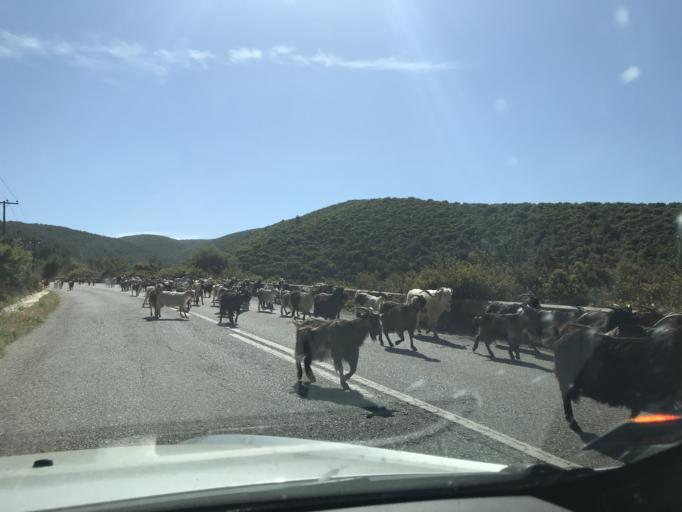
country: GR
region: Central Macedonia
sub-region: Nomos Chalkidikis
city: Sykia
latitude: 39.9621
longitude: 23.9317
